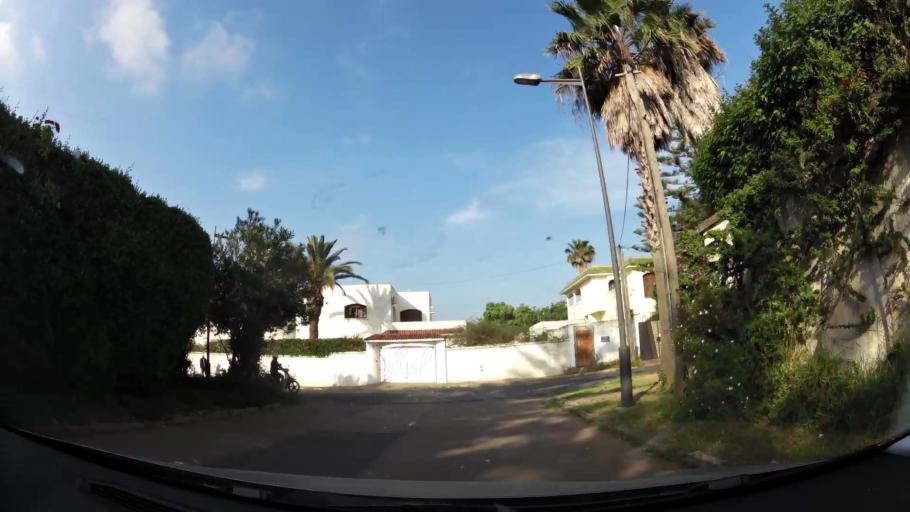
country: MA
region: Rabat-Sale-Zemmour-Zaer
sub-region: Rabat
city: Rabat
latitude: 33.9436
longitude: -6.8127
